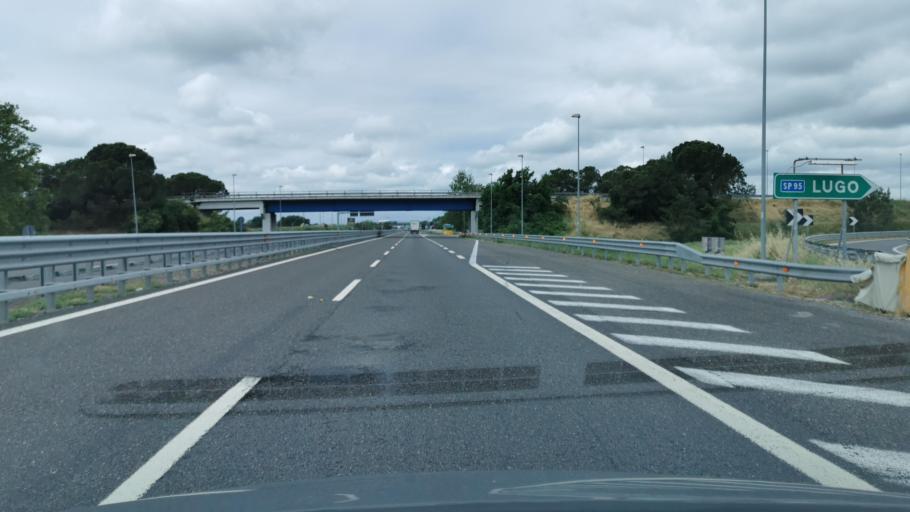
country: IT
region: Emilia-Romagna
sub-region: Provincia di Ravenna
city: Cotignola
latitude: 44.3912
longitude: 11.9259
